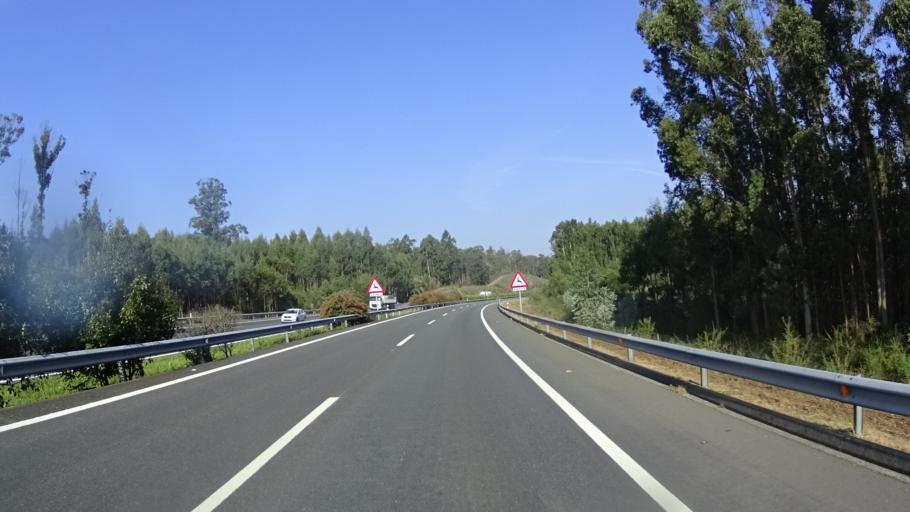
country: ES
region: Galicia
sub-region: Provincia da Coruna
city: Irixoa
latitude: 43.2361
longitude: -8.0870
